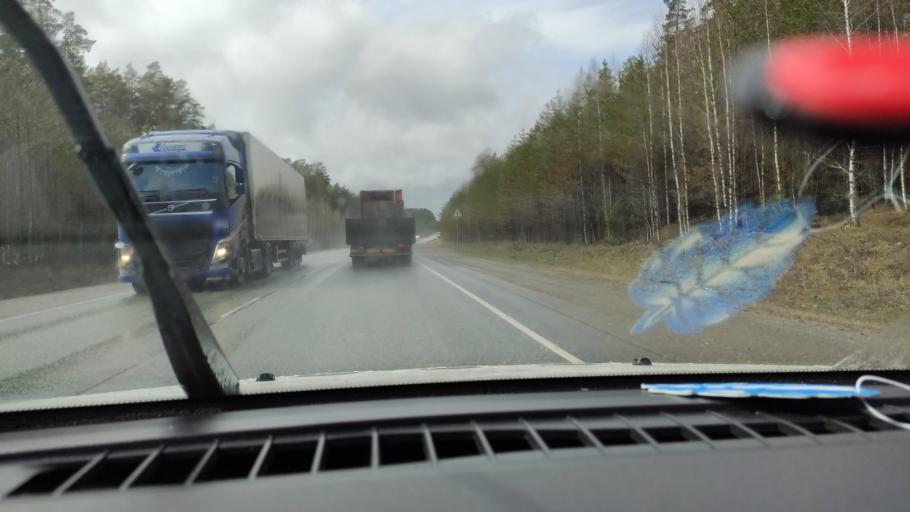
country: RU
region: Sverdlovsk
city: Achit
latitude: 56.7798
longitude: 57.9431
